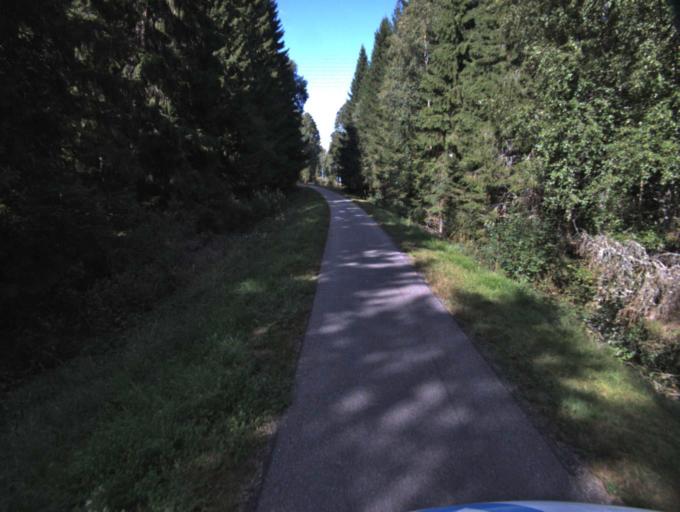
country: SE
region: Vaestra Goetaland
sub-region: Ulricehamns Kommun
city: Ulricehamn
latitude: 57.8291
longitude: 13.3450
